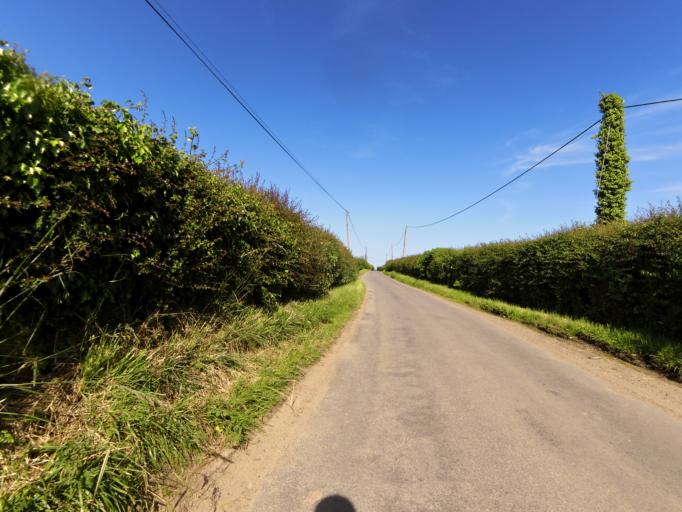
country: GB
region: England
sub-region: Suffolk
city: Felixstowe
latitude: 51.9780
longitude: 1.3650
